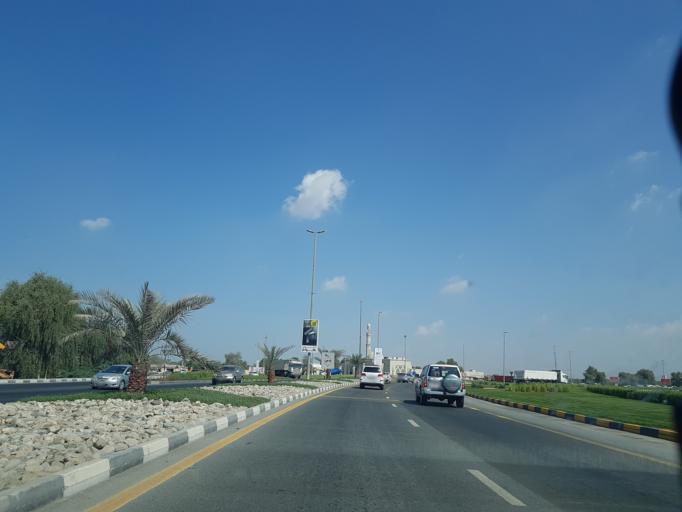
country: AE
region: Ra's al Khaymah
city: Ras al-Khaimah
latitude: 25.7121
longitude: 55.9703
